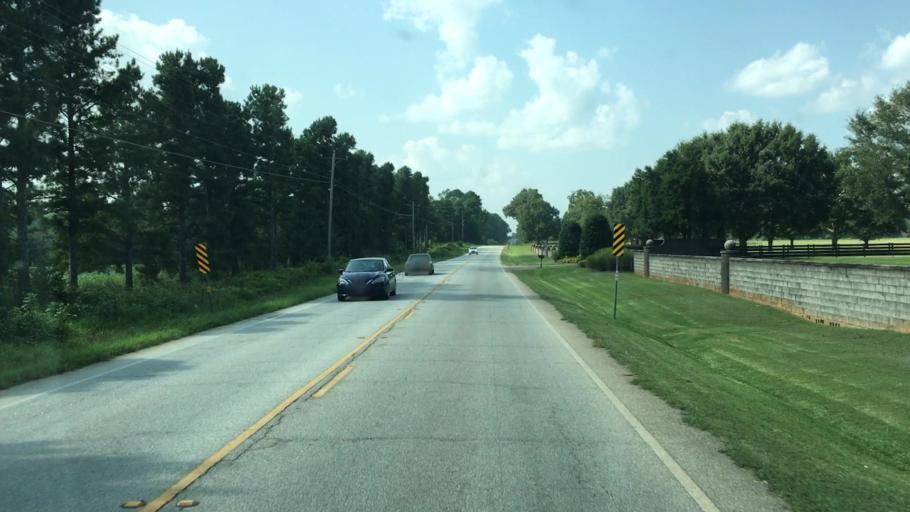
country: US
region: Georgia
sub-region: Walton County
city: Social Circle
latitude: 33.5676
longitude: -83.7388
